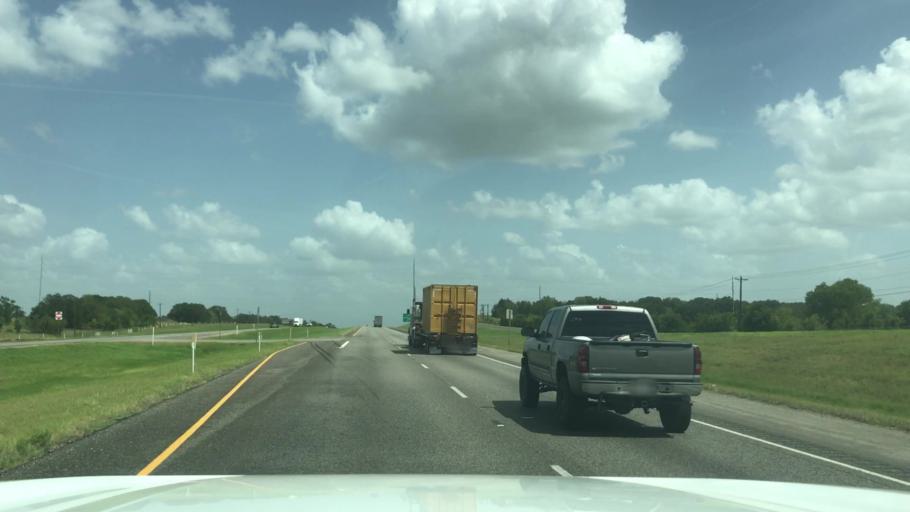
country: US
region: Texas
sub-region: Brazos County
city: Bryan
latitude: 30.7422
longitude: -96.4475
